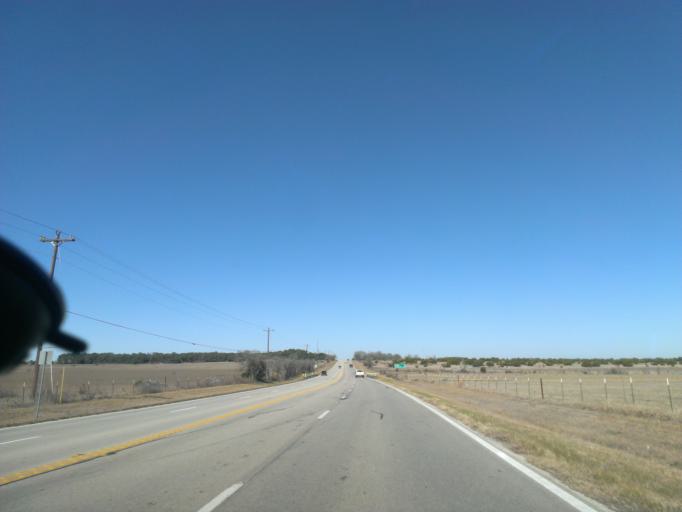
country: US
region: Texas
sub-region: Williamson County
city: Florence
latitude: 30.7766
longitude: -97.8774
